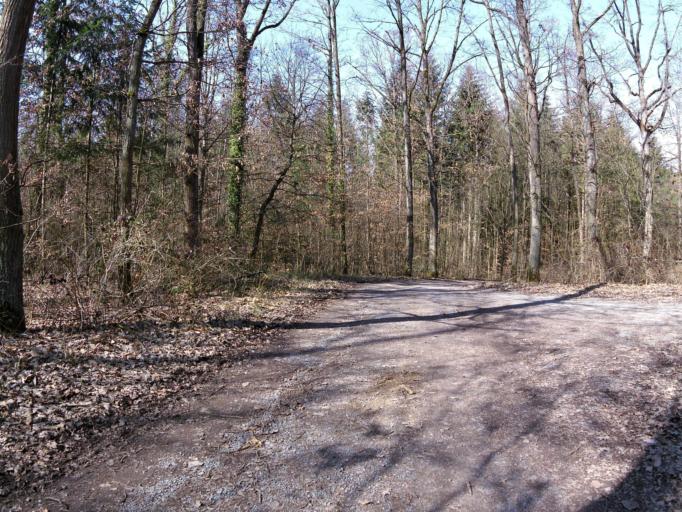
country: DE
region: Bavaria
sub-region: Regierungsbezirk Unterfranken
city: Rottendorf
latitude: 49.8094
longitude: 10.0202
